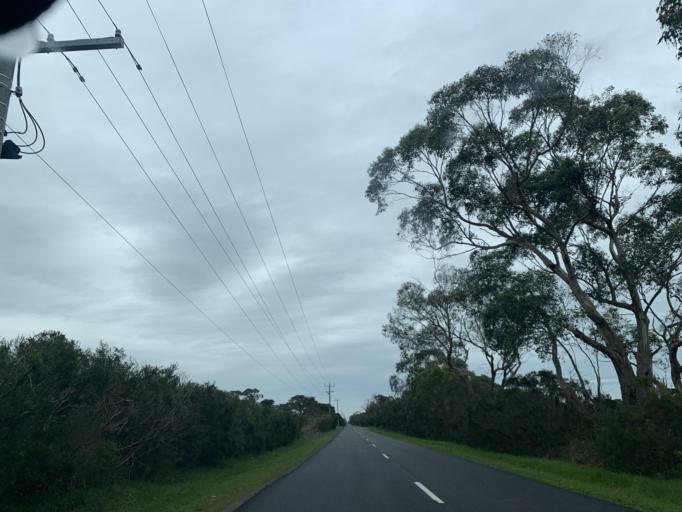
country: AU
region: Victoria
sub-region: Cardinia
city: Garfield
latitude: -38.0829
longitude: 145.5886
